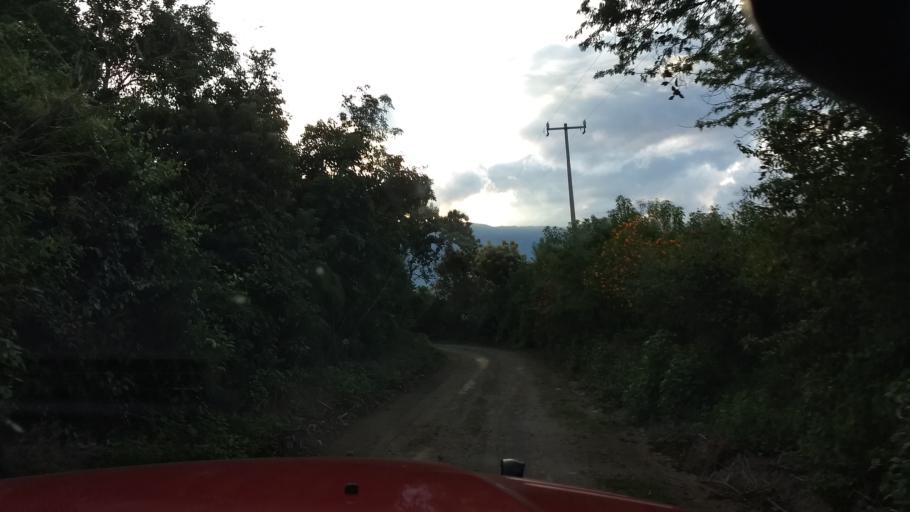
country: MX
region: Colima
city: Suchitlan
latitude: 19.4951
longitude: -103.7785
